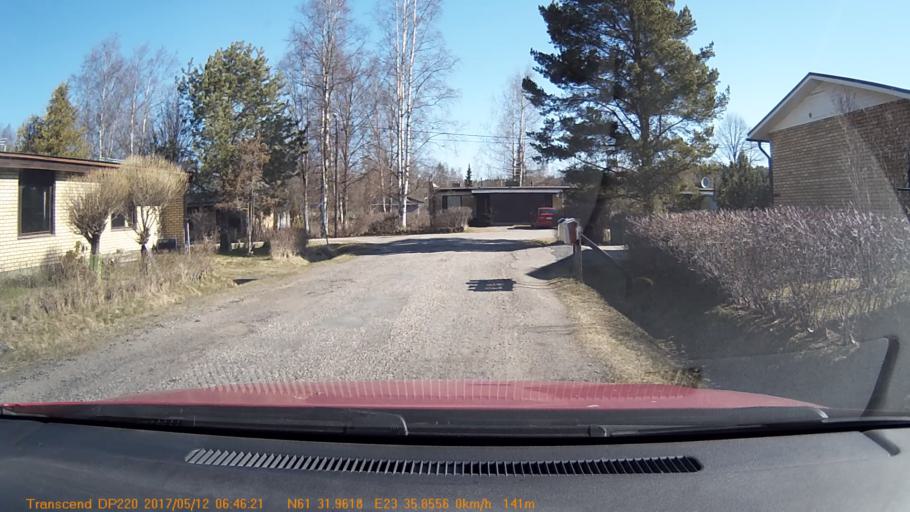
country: FI
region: Pirkanmaa
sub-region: Tampere
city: Yloejaervi
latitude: 61.5327
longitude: 23.5976
